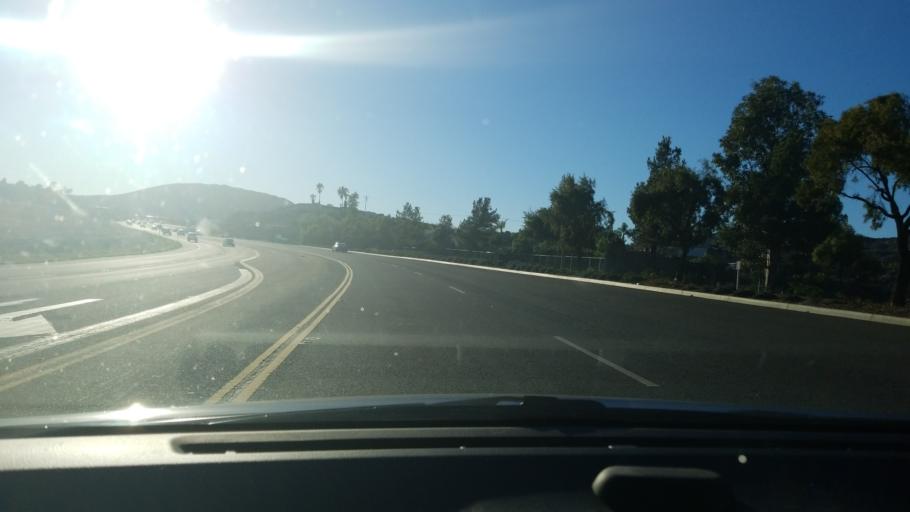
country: US
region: California
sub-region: Riverside County
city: Green Acres
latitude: 33.7436
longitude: -117.0615
